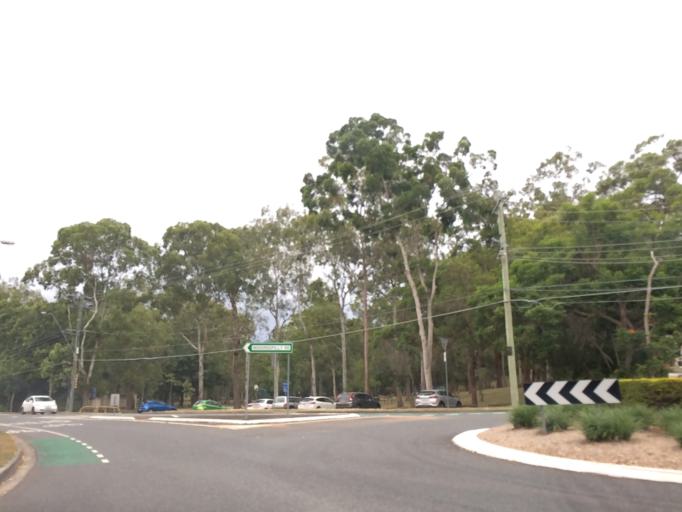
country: AU
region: Queensland
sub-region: Brisbane
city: Taringa
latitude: -27.5021
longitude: 152.9911
